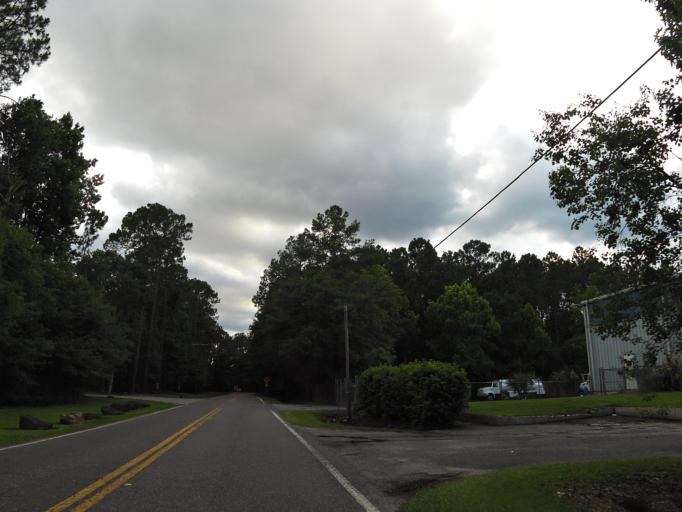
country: US
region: Florida
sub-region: Duval County
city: Jacksonville
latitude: 30.3174
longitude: -81.7648
